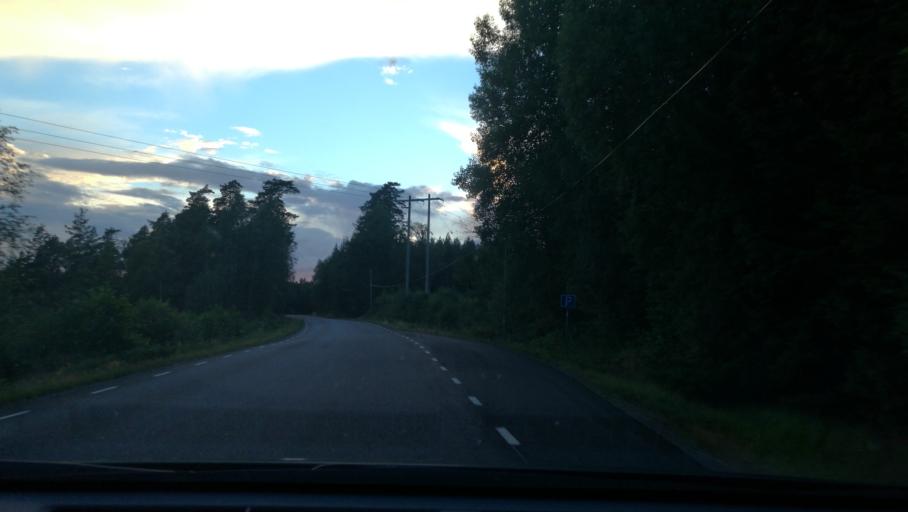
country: SE
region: OEstergoetland
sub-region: Norrkopings Kommun
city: Jursla
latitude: 58.8063
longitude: 16.1062
